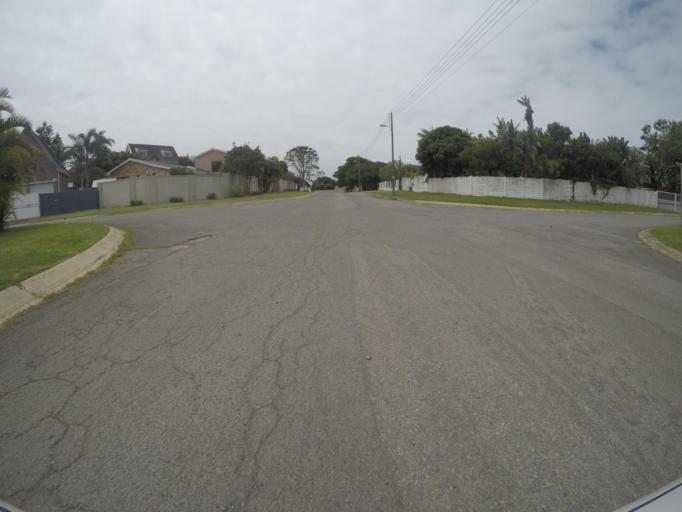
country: ZA
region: Eastern Cape
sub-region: Buffalo City Metropolitan Municipality
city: East London
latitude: -32.9797
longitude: 27.9499
